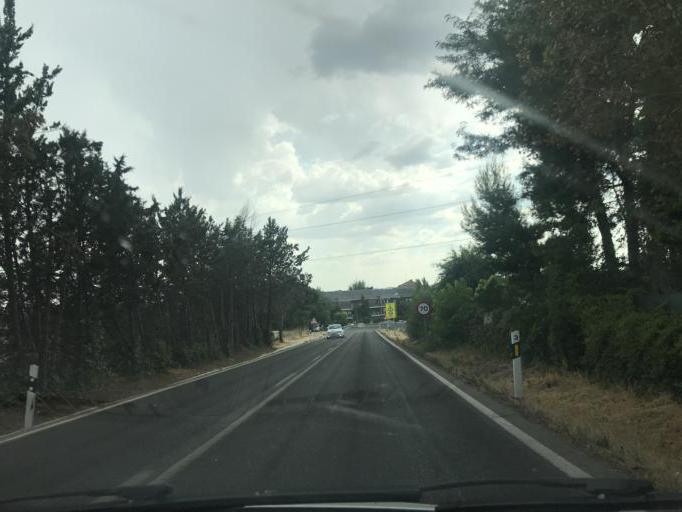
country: ES
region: Madrid
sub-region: Provincia de Madrid
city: Paracuellos de Jarama
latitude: 40.5007
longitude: -3.5434
